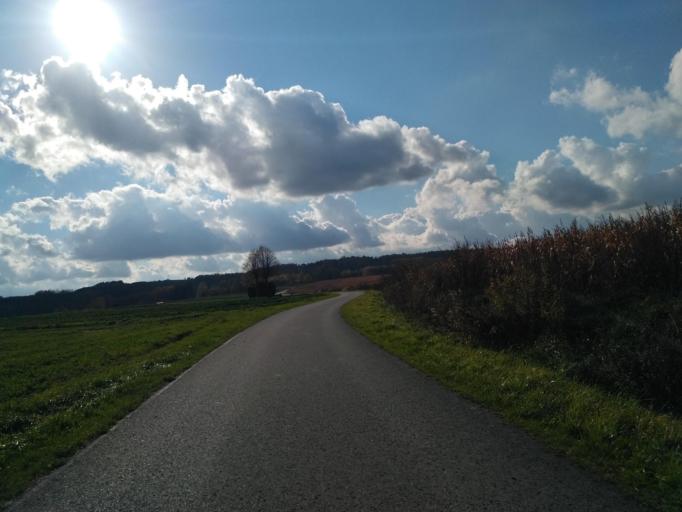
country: PL
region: Subcarpathian Voivodeship
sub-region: Powiat rzeszowski
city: Zglobien
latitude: 49.9929
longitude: 21.8509
